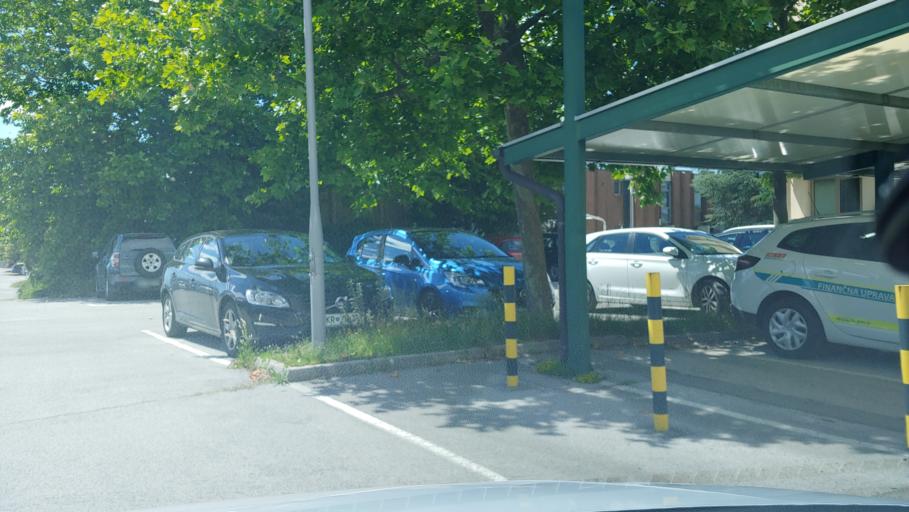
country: SI
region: Sezana
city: Sezana
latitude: 45.7021
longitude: 13.8490
